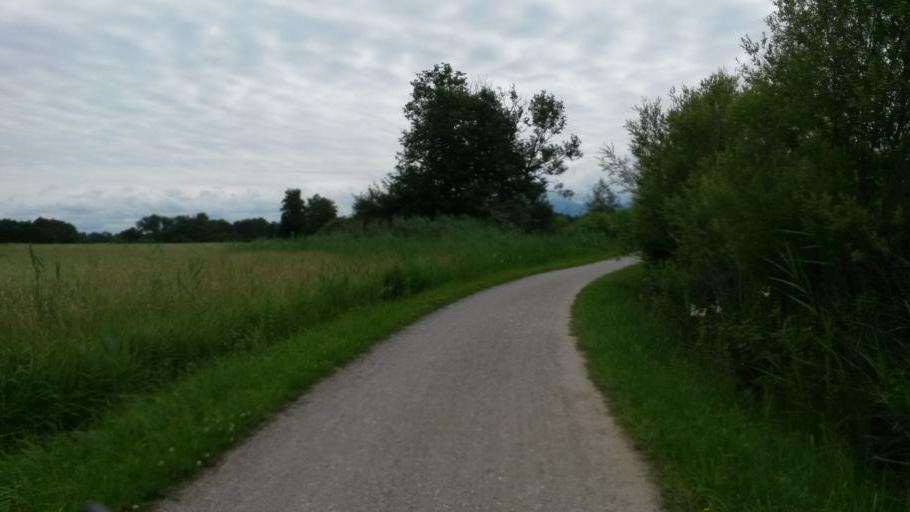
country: DE
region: Bavaria
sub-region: Upper Bavaria
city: Rimsting
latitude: 47.8866
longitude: 12.3606
